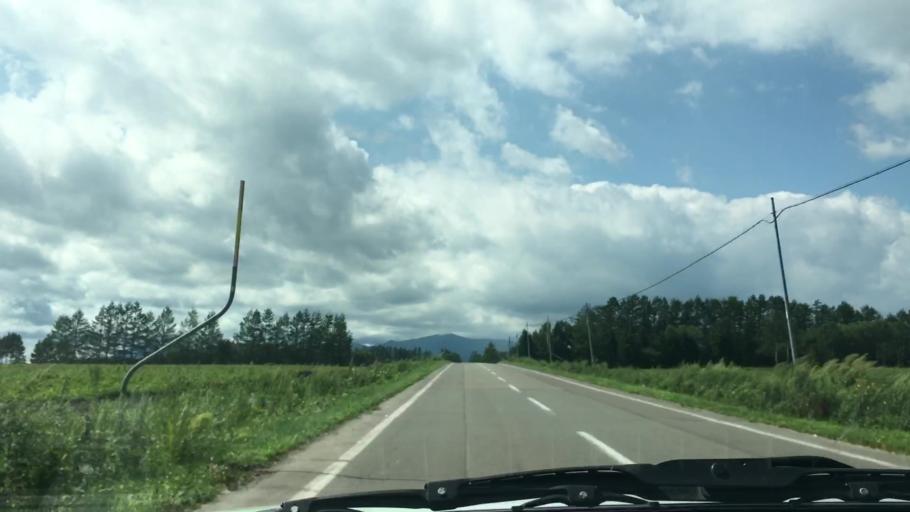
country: JP
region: Hokkaido
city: Otofuke
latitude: 43.2774
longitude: 143.3635
